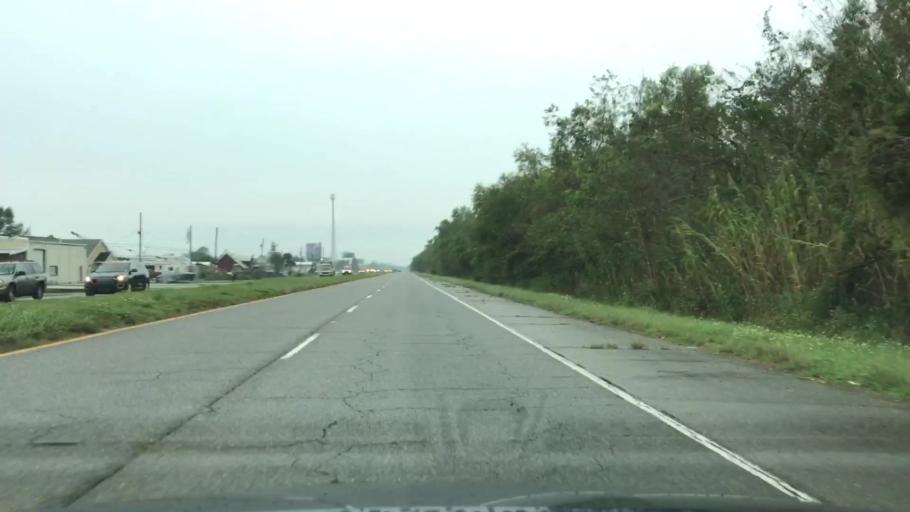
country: US
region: Louisiana
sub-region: Saint Charles Parish
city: Des Allemands
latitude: 29.8140
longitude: -90.4900
